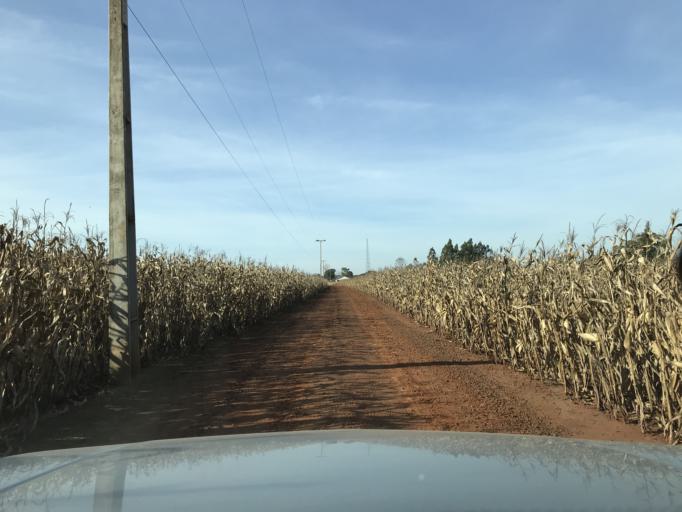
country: BR
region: Parana
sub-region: Palotina
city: Palotina
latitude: -24.2501
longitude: -53.7512
